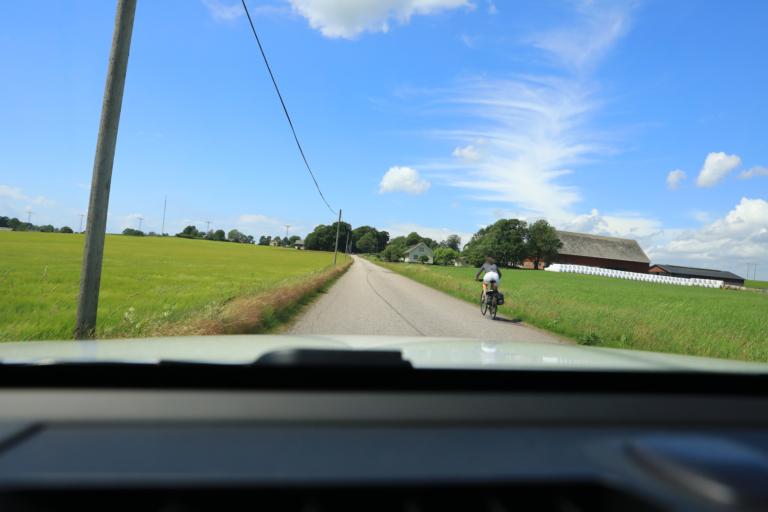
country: SE
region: Halland
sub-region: Varbergs Kommun
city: Tvaaker
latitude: 57.1106
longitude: 12.4348
